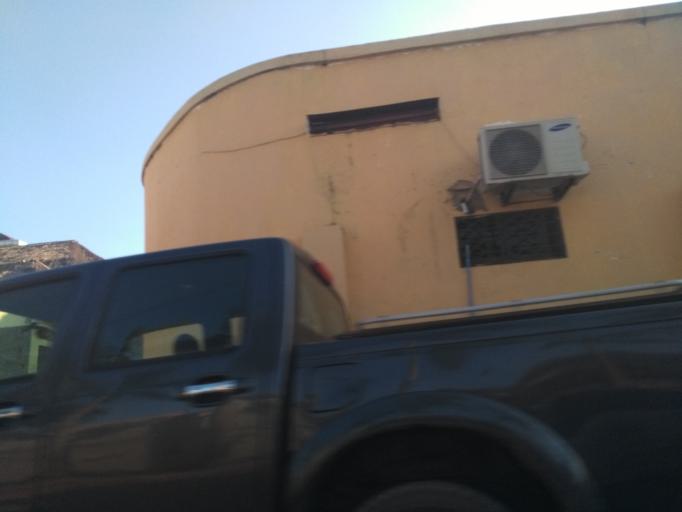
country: TZ
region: Dar es Salaam
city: Magomeni
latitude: -6.7611
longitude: 39.2540
